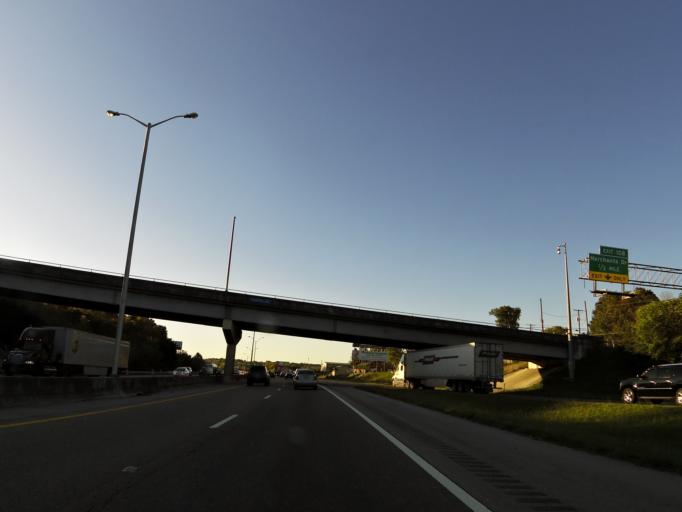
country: US
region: Tennessee
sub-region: Knox County
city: Knoxville
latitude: 36.0032
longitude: -83.9619
